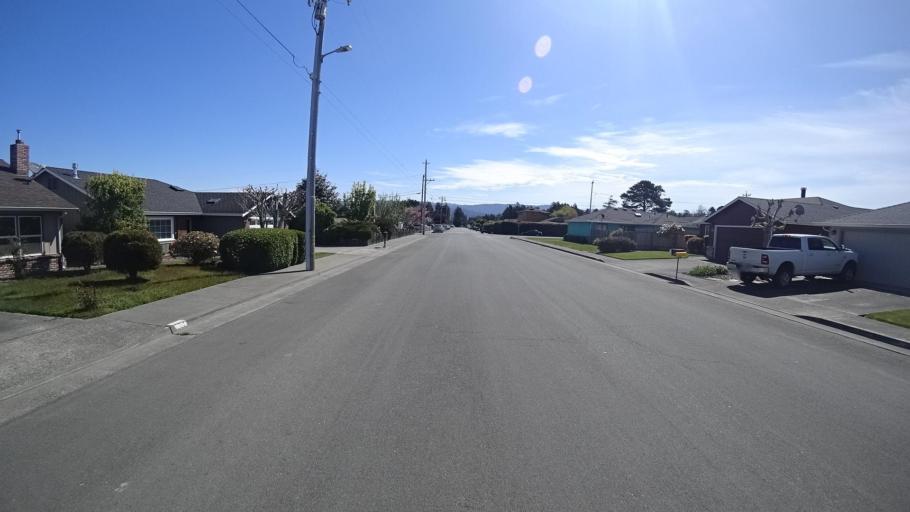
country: US
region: California
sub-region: Humboldt County
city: Myrtletown
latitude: 40.7865
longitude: -124.1291
